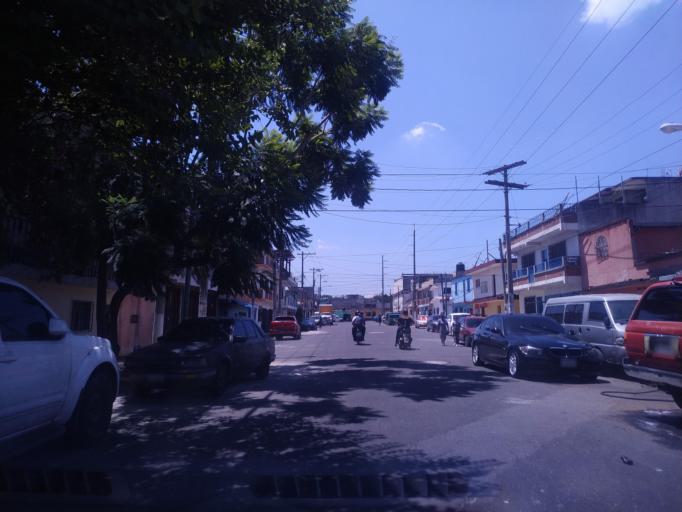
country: GT
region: Guatemala
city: Mixco
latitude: 14.6790
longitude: -90.5704
